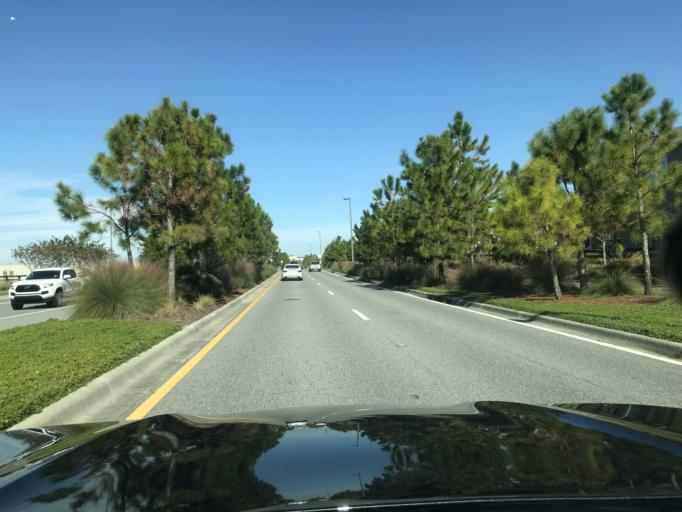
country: US
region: Florida
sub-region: Orange County
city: Oakland
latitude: 28.4661
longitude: -81.6272
